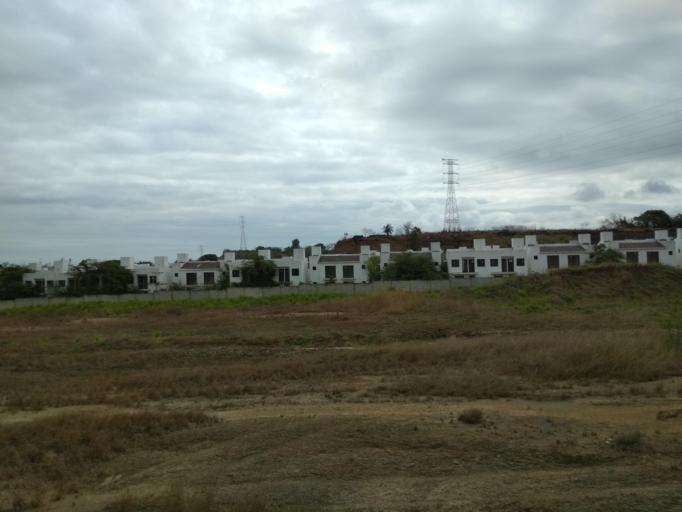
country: MX
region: Veracruz
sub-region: Medellin
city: Fraccionamiento Arboledas San Ramon
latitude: 19.0873
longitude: -96.1358
